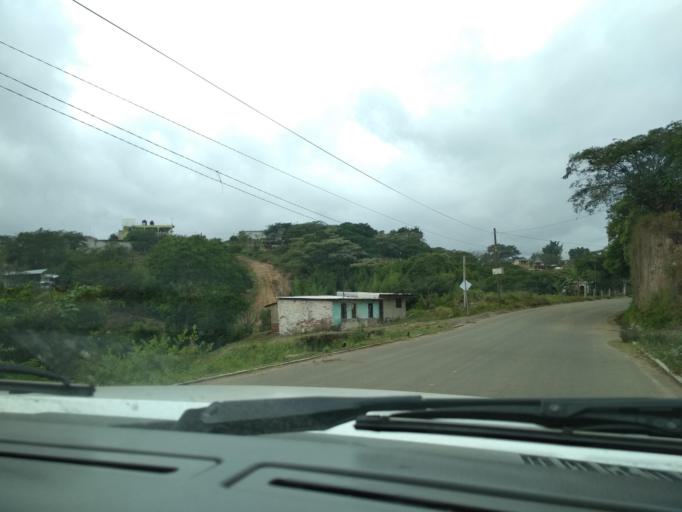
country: MX
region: Veracruz
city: El Castillo
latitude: 19.5484
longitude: -96.8493
